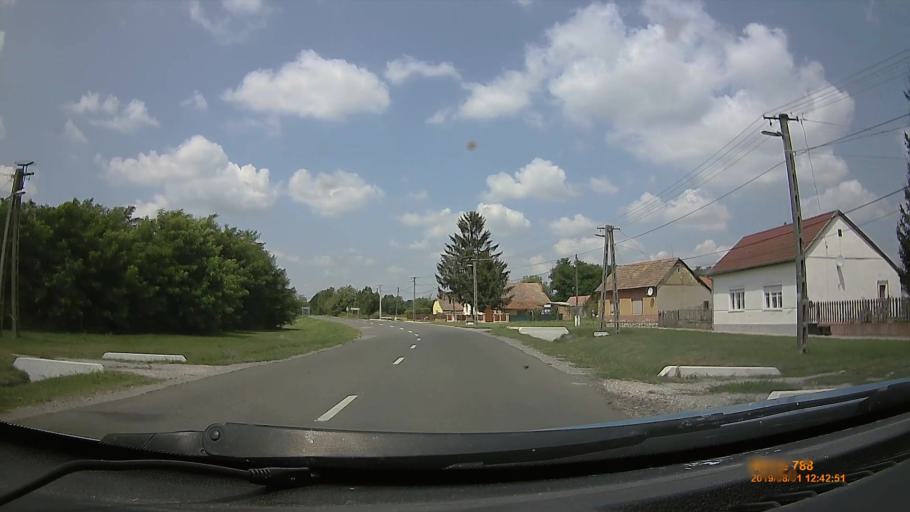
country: HU
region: Baranya
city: Harkany
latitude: 45.8377
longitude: 18.1605
